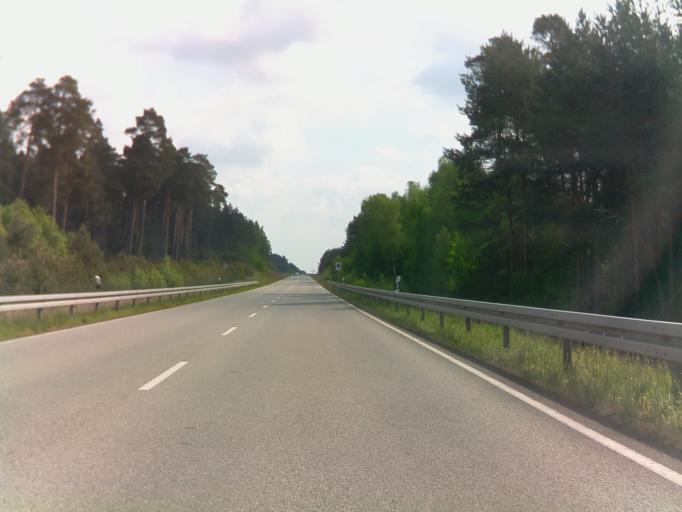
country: DE
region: Saxony-Anhalt
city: Uchtspringe
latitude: 52.5374
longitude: 11.5717
